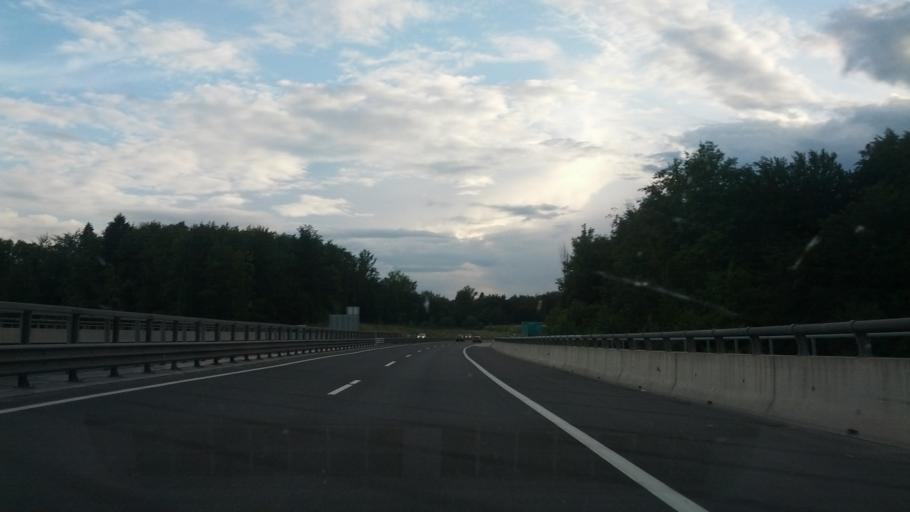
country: SI
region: Skocjan
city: Skocjan
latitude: 45.8503
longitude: 15.2415
